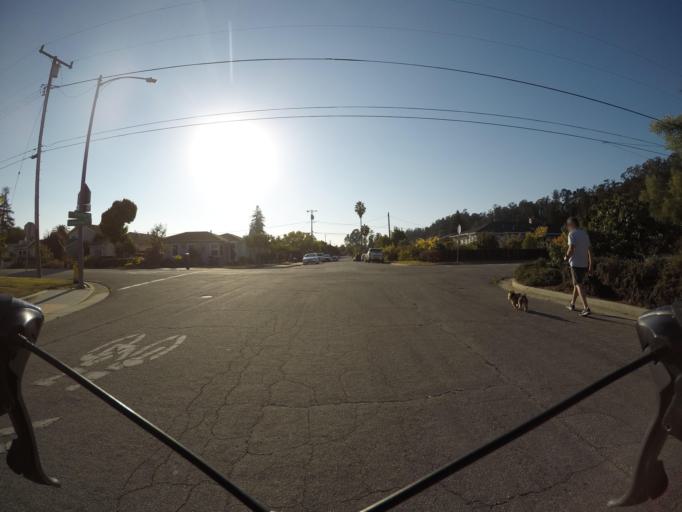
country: US
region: California
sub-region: Santa Cruz County
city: Live Oak
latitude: 36.9901
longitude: -121.9985
